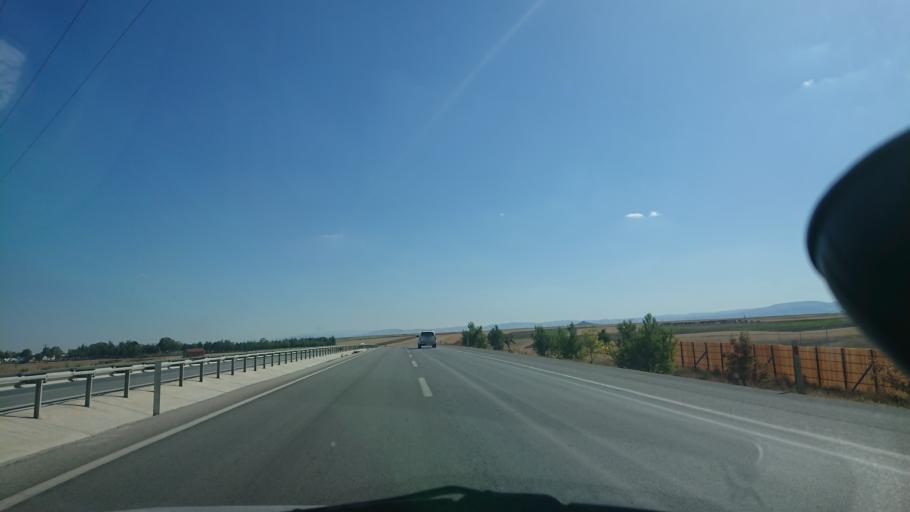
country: TR
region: Eskisehir
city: Mahmudiye
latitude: 39.5075
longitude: 30.9651
